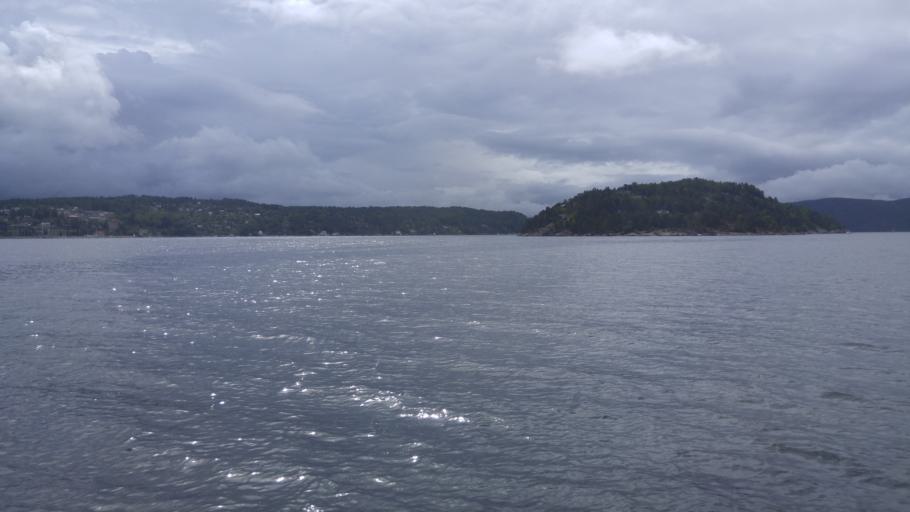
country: NO
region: Akershus
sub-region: Nesodden
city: Fagerstrand
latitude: 59.7368
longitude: 10.5689
